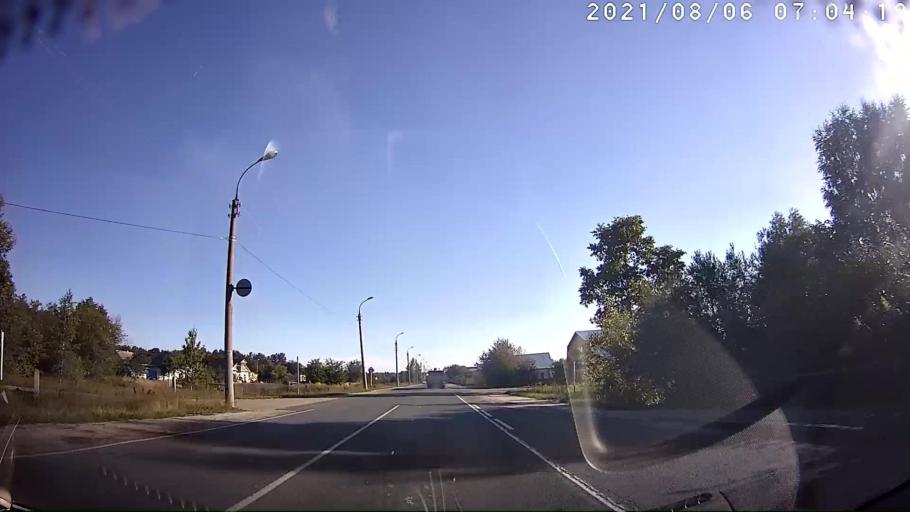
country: RU
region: Mariy-El
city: Yoshkar-Ola
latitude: 56.5461
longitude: 47.9817
